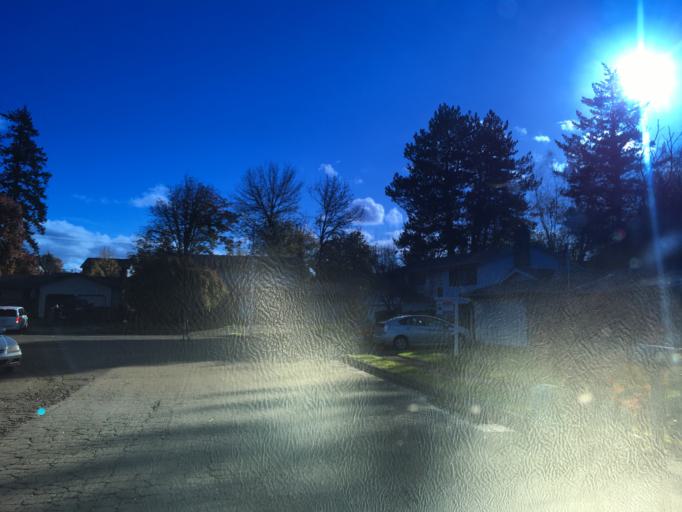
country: US
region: Oregon
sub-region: Multnomah County
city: Troutdale
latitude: 45.5059
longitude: -122.3943
